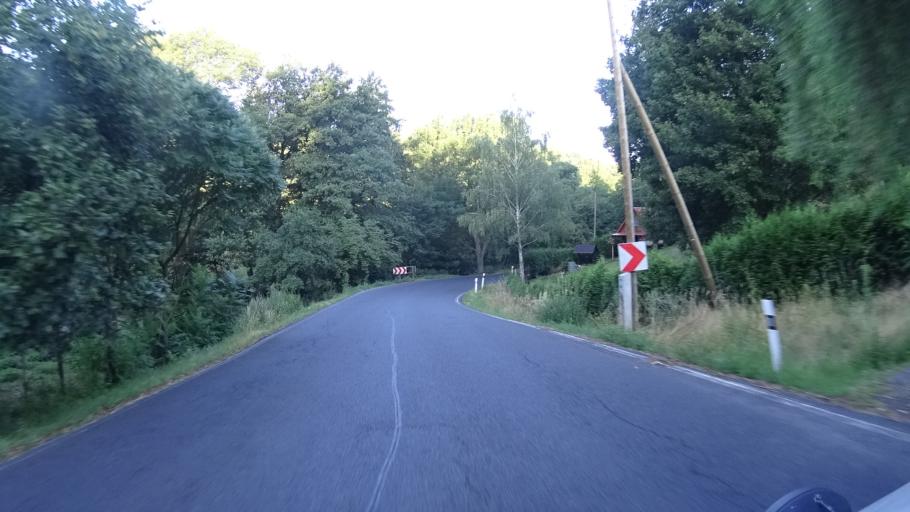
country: CZ
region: Ustecky
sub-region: Okres Litomerice
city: Litomerice
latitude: 50.5807
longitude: 14.0845
